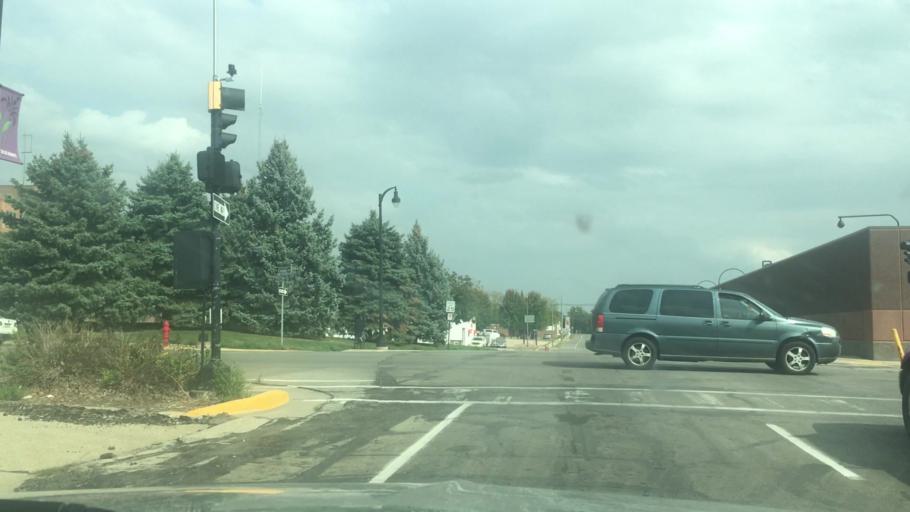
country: US
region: Iowa
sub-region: Marshall County
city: Marshalltown
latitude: 42.0467
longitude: -92.9132
